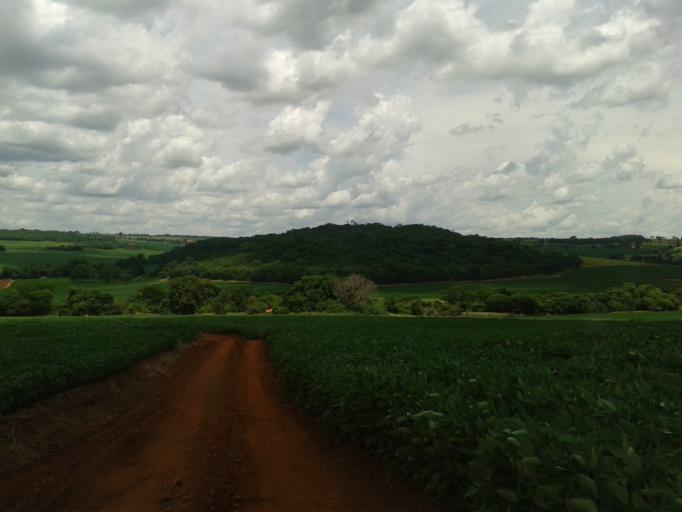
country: BR
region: Minas Gerais
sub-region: Centralina
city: Centralina
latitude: -18.6841
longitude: -49.2198
